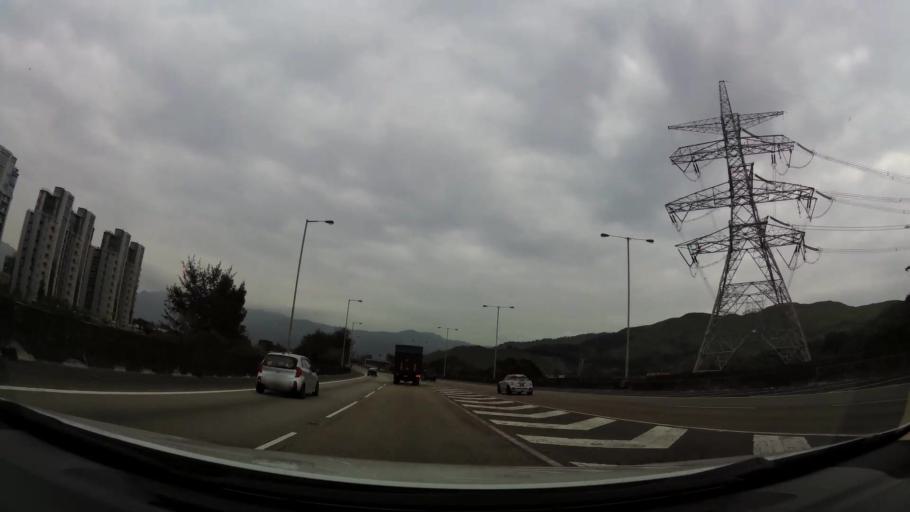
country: HK
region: Yuen Long
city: Yuen Long Kau Hui
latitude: 22.4422
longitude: 114.0521
